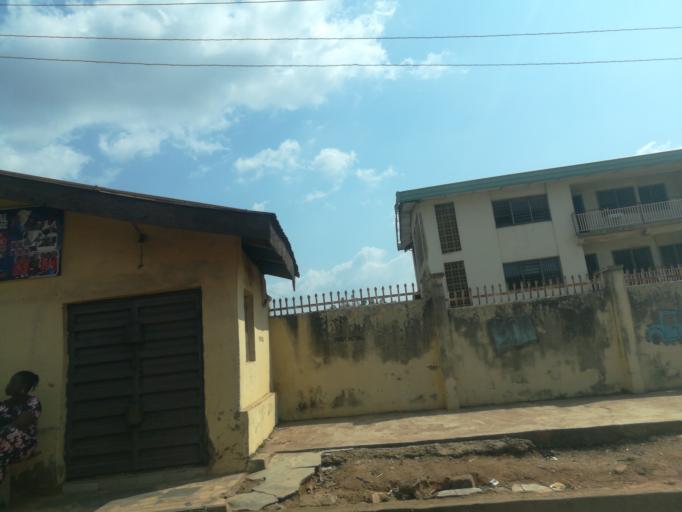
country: NG
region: Oyo
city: Moniya
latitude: 7.5219
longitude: 3.9127
